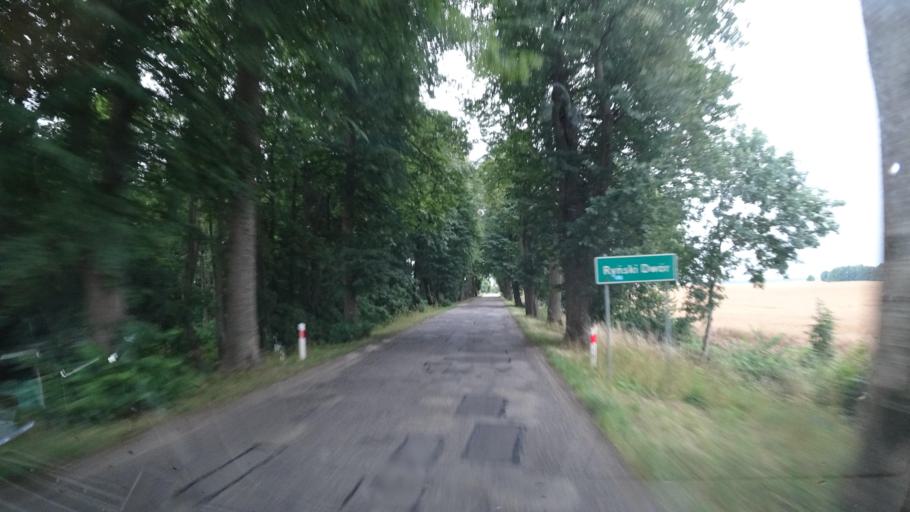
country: PL
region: Warmian-Masurian Voivodeship
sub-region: Powiat gizycki
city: Ryn
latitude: 53.9259
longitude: 21.5516
